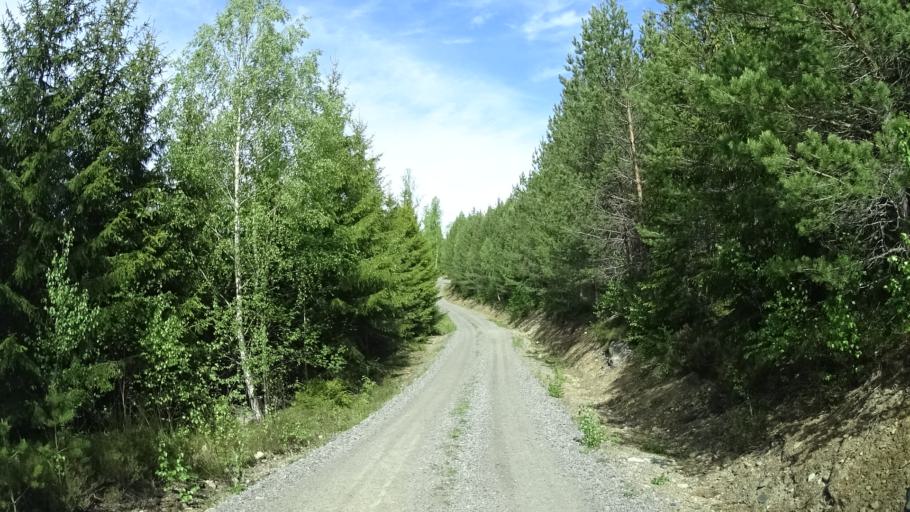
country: SE
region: OEstergoetland
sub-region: Finspangs Kommun
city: Finspang
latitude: 58.7947
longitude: 15.8553
